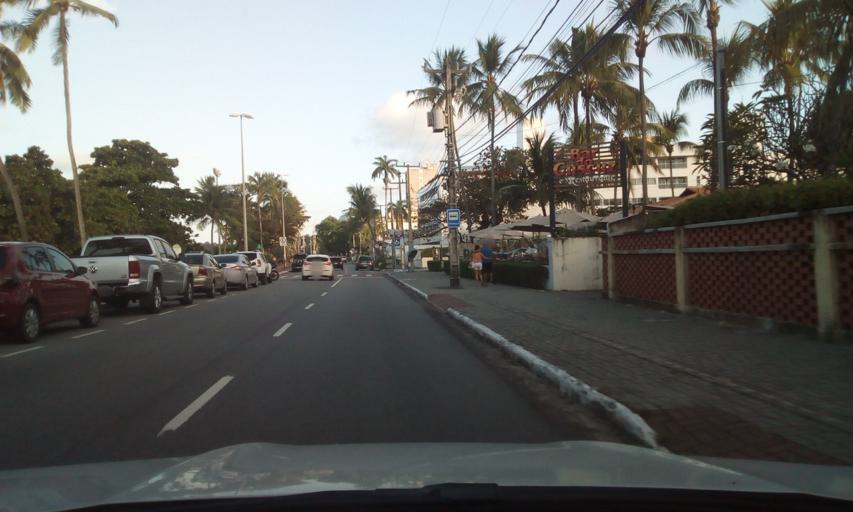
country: BR
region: Paraiba
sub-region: Joao Pessoa
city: Joao Pessoa
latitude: -7.1361
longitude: -34.8196
